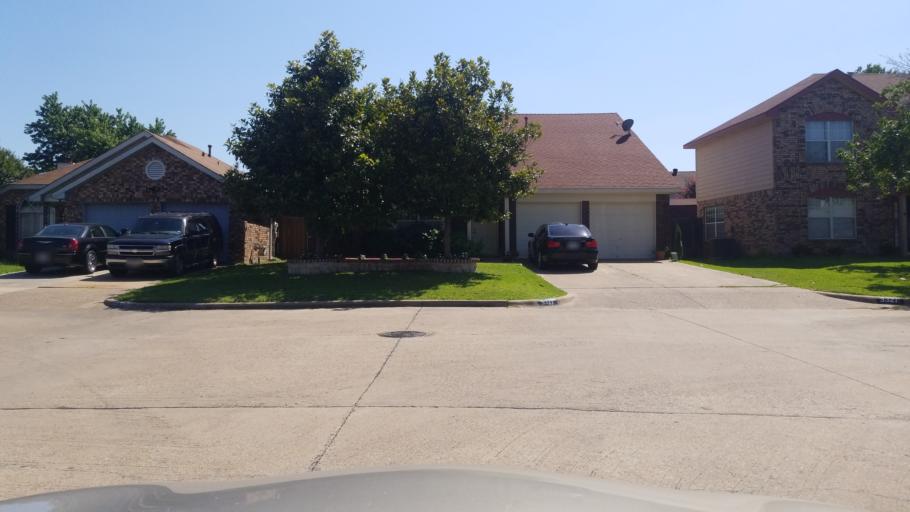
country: US
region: Texas
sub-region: Dallas County
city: Grand Prairie
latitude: 32.6910
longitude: -97.0104
